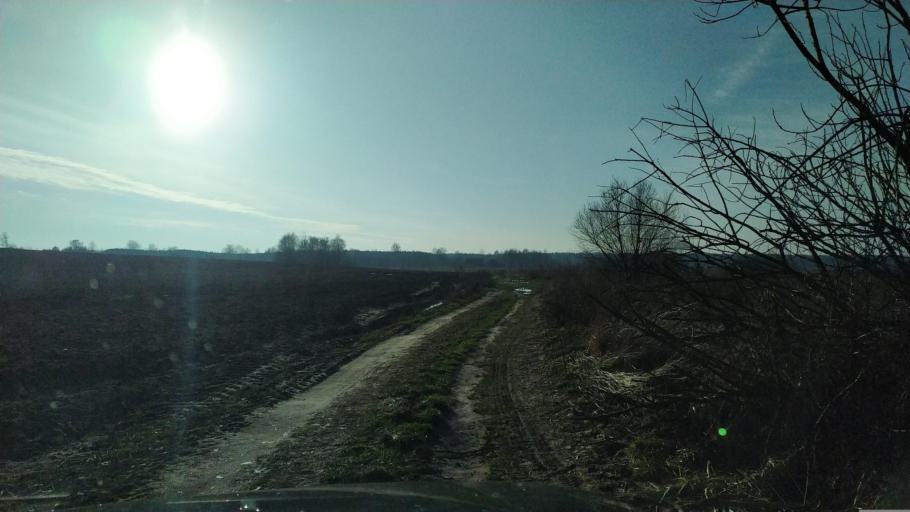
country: BY
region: Brest
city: Kamyanyets
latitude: 52.3785
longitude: 23.7775
